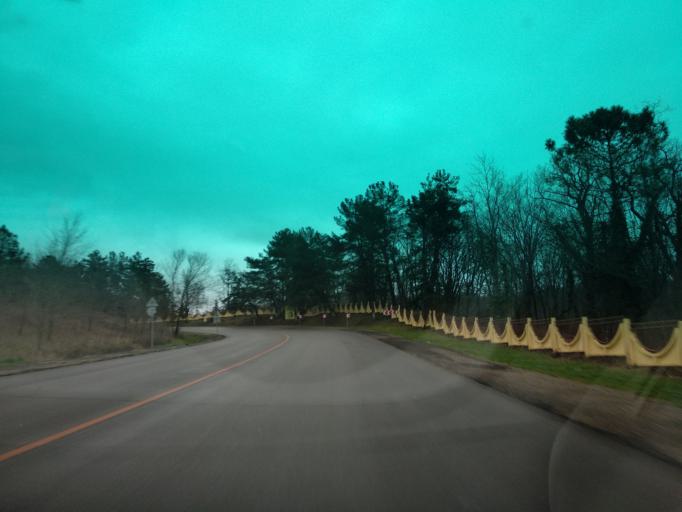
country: RU
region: Krasnodarskiy
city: Novomikhaylovskiy
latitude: 44.2594
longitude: 38.8229
